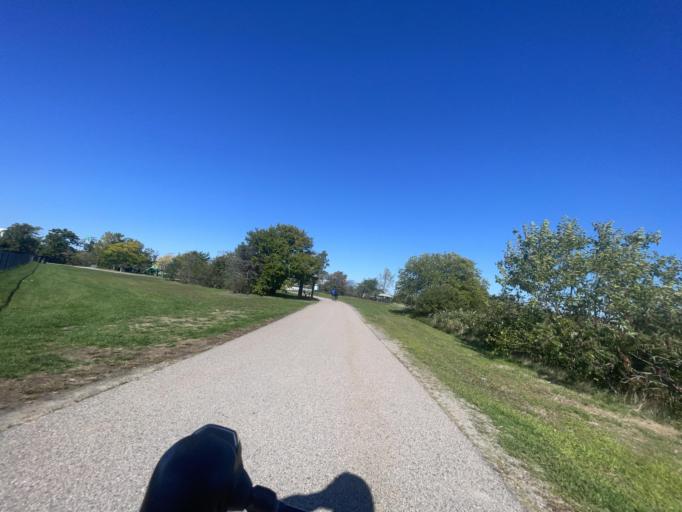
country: US
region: Massachusetts
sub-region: Norfolk County
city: Milton
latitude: 42.2830
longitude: -71.0419
